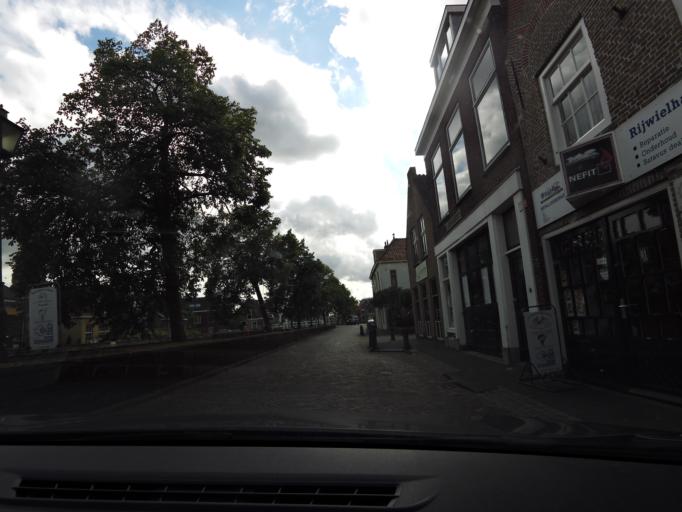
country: NL
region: South Holland
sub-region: Gemeente Delft
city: Delft
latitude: 51.9776
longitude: 4.3169
